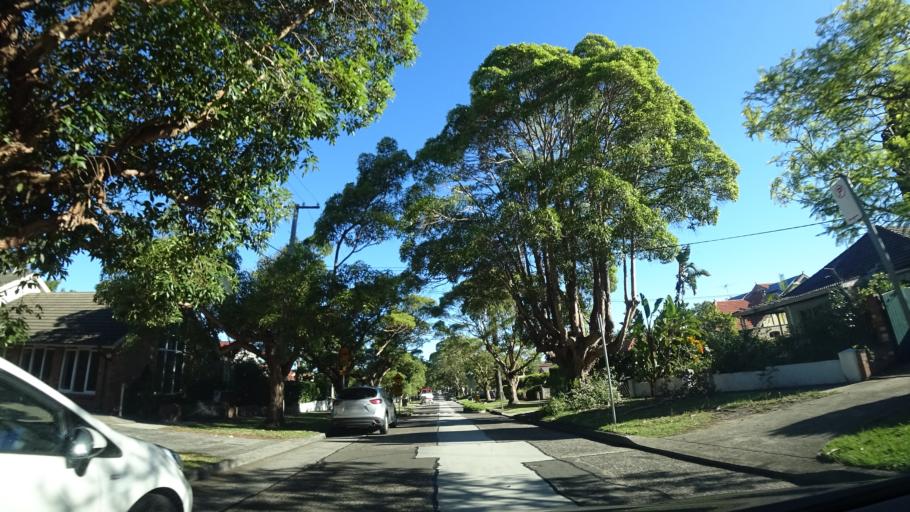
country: AU
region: New South Wales
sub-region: Ku-ring-gai
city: Roseville Chase
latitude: -33.7867
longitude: 151.1890
